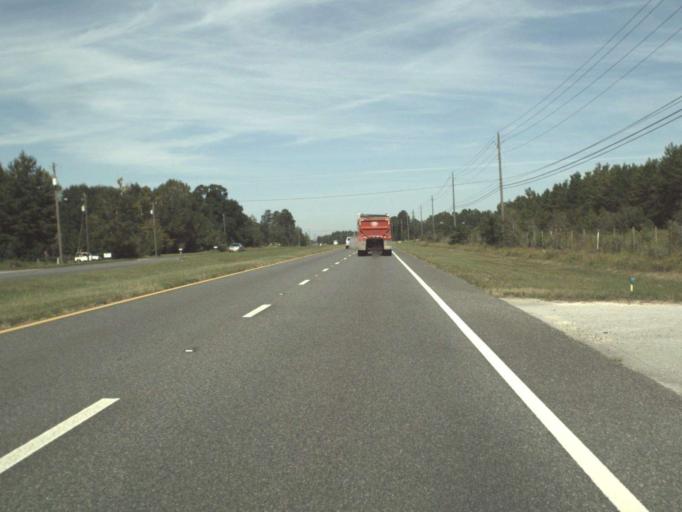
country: US
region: Florida
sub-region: Bay County
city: Lynn Haven
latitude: 30.3743
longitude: -85.6771
